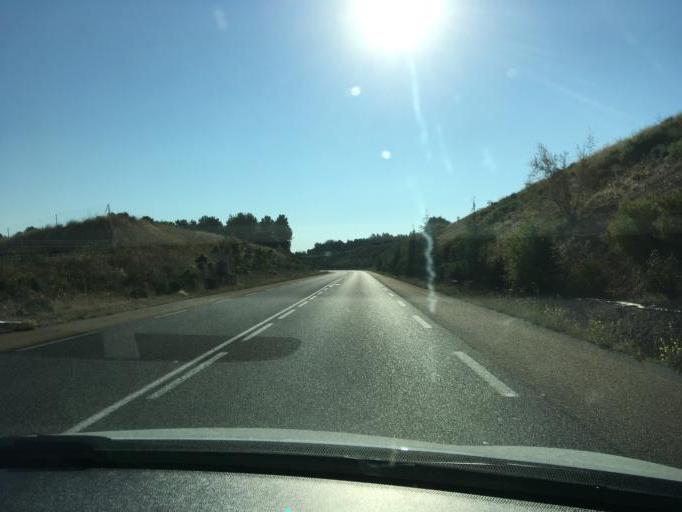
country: FR
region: Provence-Alpes-Cote d'Azur
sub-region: Departement des Bouches-du-Rhone
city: Charleval
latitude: 43.7119
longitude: 5.2342
